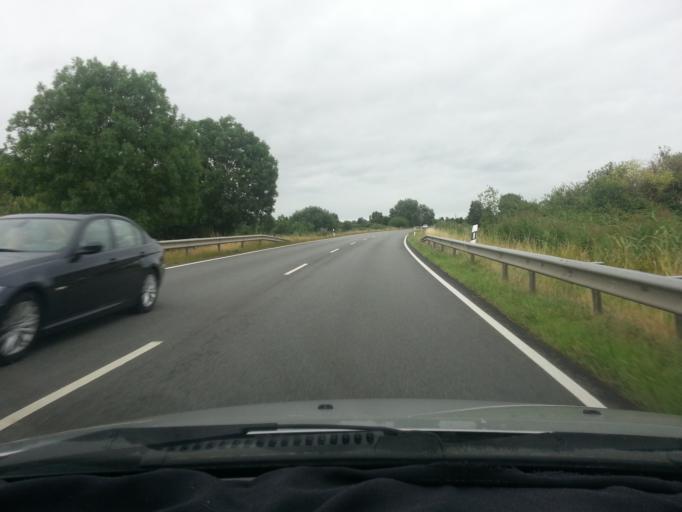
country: DE
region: Rheinland-Pfalz
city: Niederkirchen bei Deidesheim
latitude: 49.4059
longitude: 8.2054
